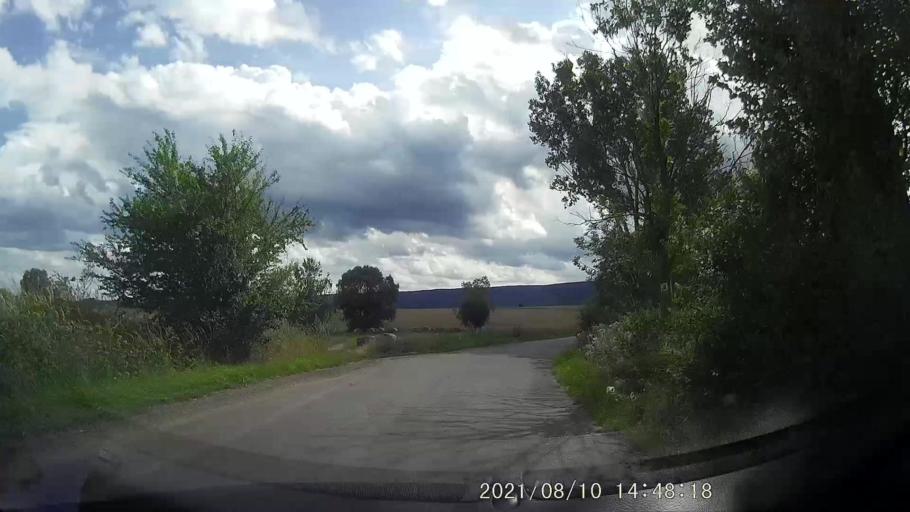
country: PL
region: Lower Silesian Voivodeship
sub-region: Powiat klodzki
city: Radkow
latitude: 50.5170
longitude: 16.4073
